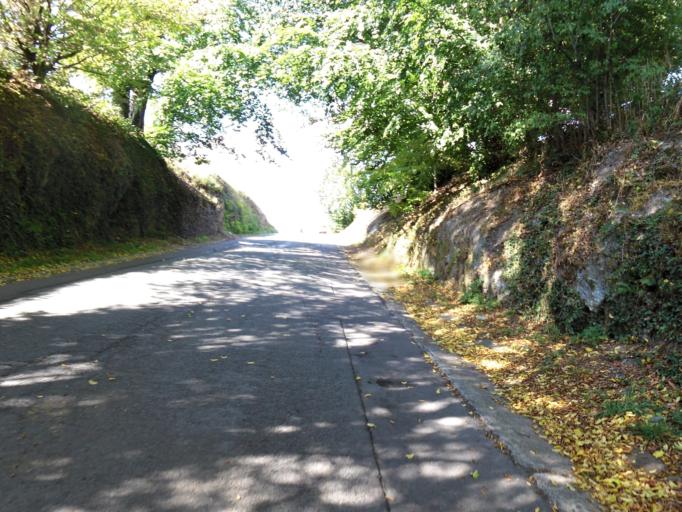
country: BE
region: Wallonia
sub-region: Province de Namur
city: Bievre
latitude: 49.8713
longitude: 4.9825
